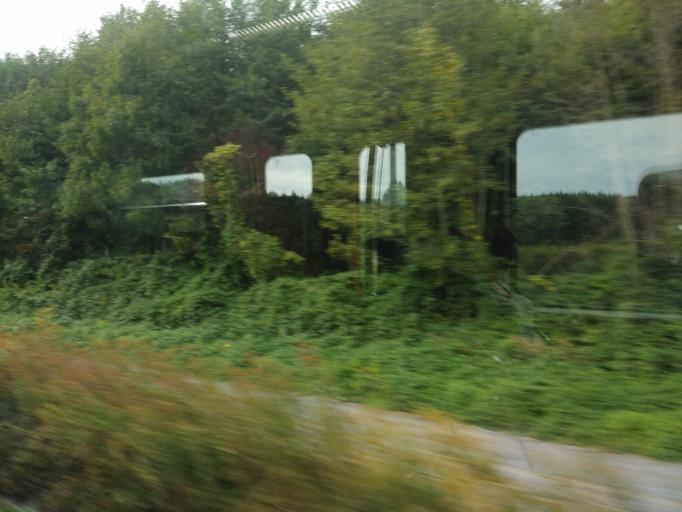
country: DE
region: Baden-Wuerttemberg
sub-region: Karlsruhe Region
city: Weingarten
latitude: 49.0464
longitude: 8.5091
